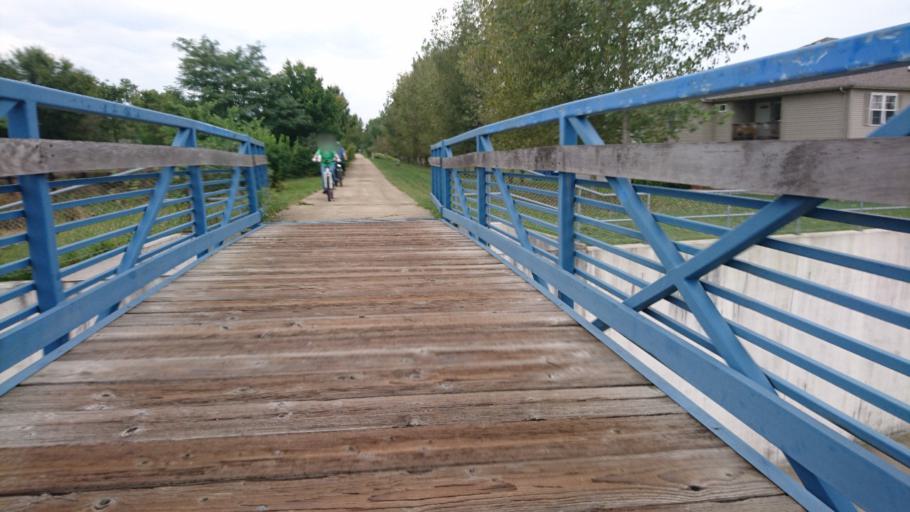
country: US
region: Illinois
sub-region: Sangamon County
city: Chatham
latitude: 39.6869
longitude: -89.6977
